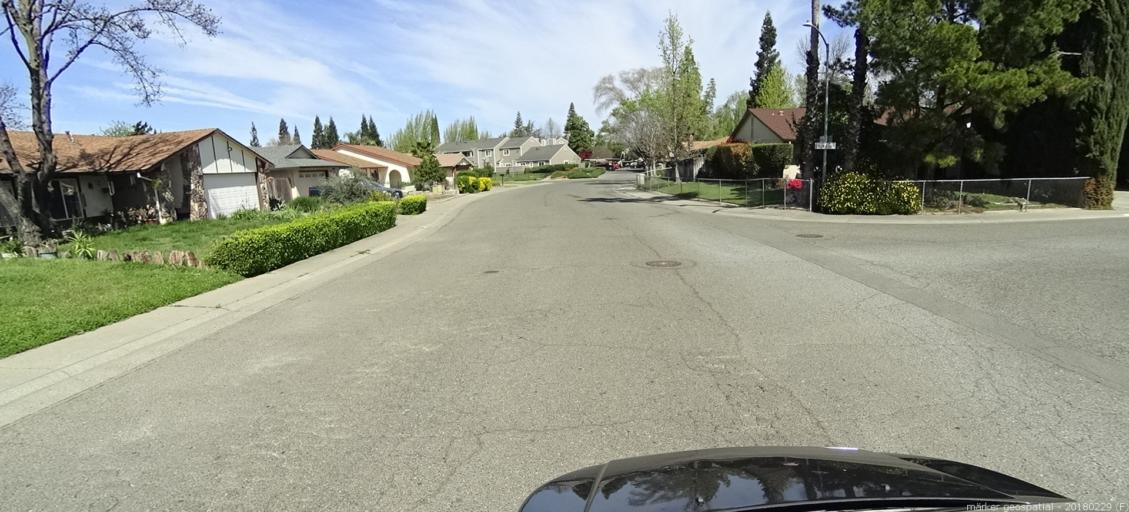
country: US
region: California
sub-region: Sacramento County
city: Rosemont
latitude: 38.5416
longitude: -121.3613
